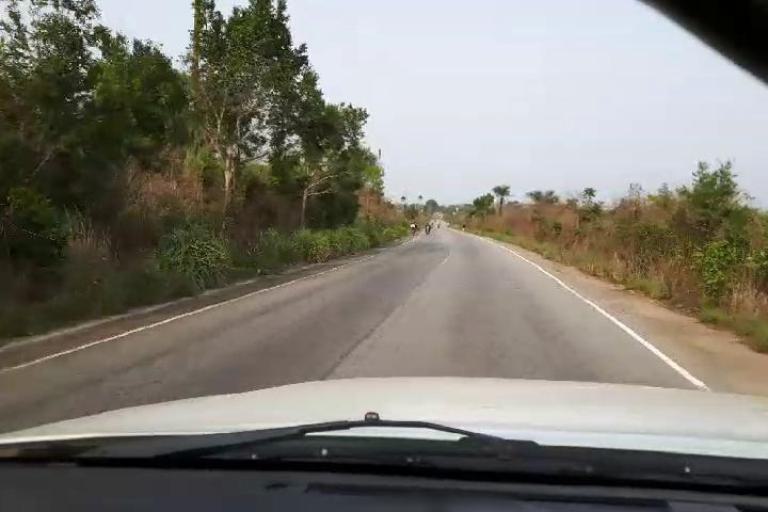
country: SL
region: Southern Province
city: Baoma
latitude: 7.9274
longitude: -11.5839
